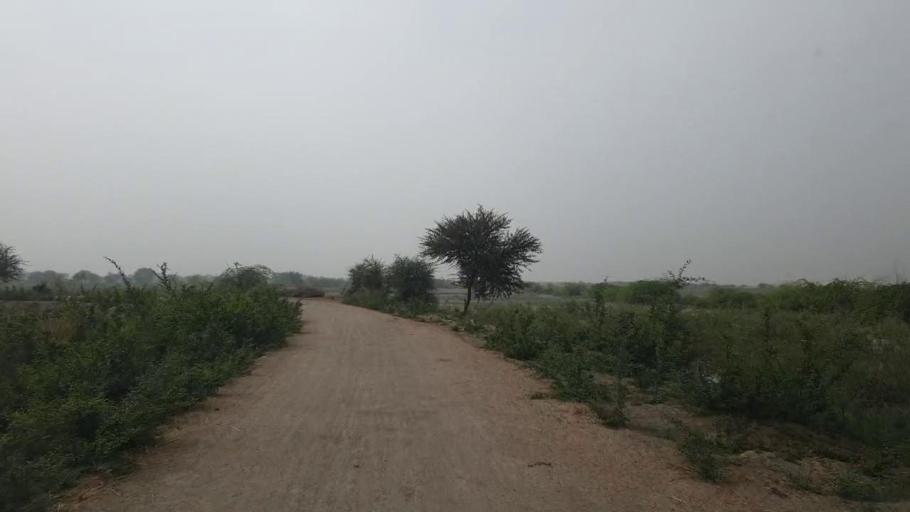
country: PK
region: Sindh
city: Badin
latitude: 24.5754
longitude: 68.6853
